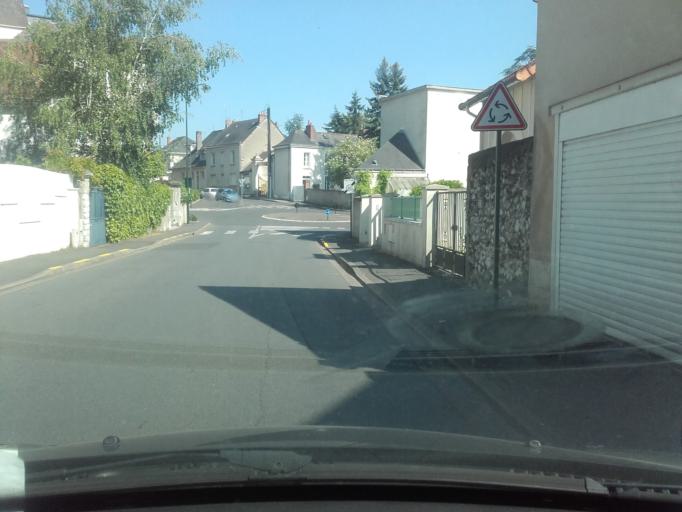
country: FR
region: Centre
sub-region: Departement d'Indre-et-Loire
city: Saint-Cyr-sur-Loire
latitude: 47.4077
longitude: 0.6787
